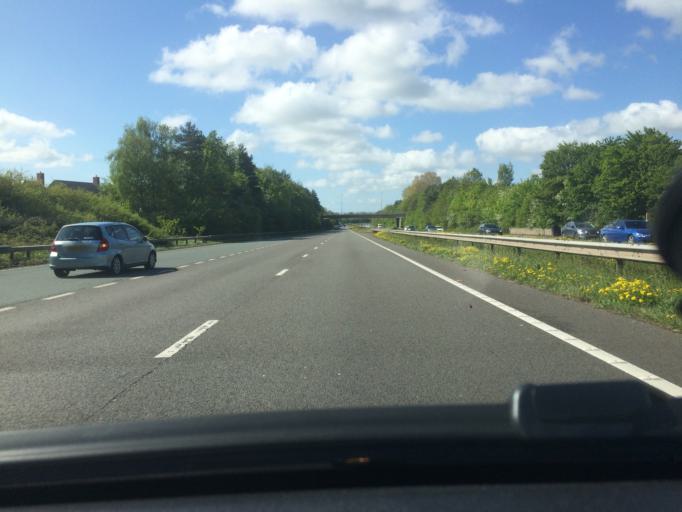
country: GB
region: England
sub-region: Cheshire West and Chester
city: Hoole
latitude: 53.1749
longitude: -2.8599
